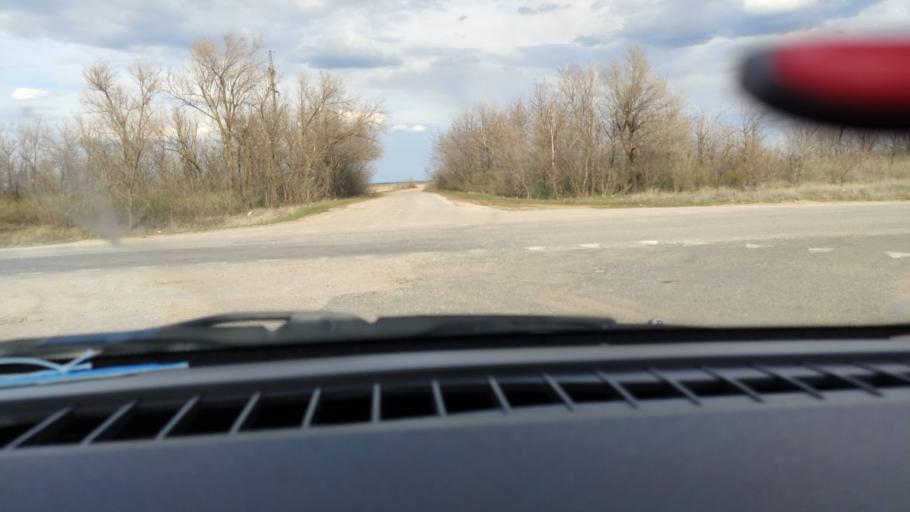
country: RU
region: Saratov
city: Rovnoye
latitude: 50.9437
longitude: 46.1268
